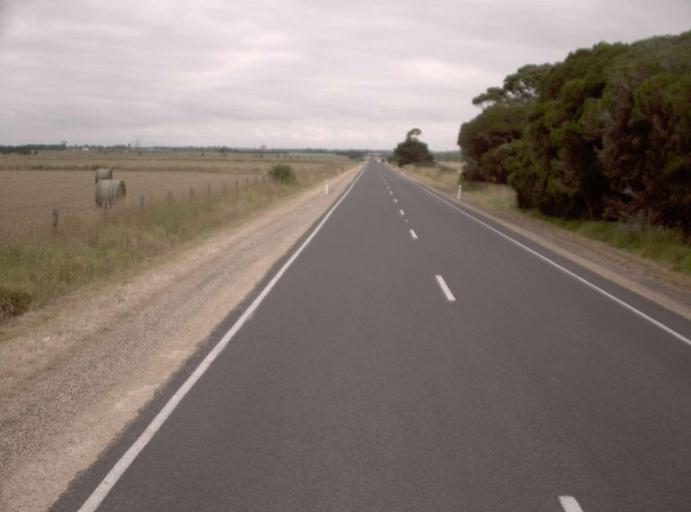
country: AU
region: Victoria
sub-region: Wellington
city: Sale
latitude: -38.0897
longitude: 146.9869
